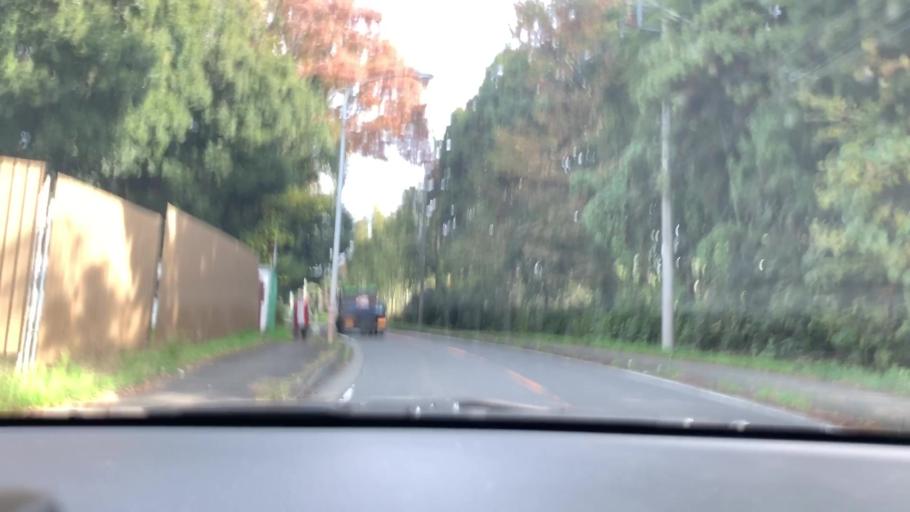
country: JP
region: Chiba
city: Nagareyama
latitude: 35.8835
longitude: 139.9059
